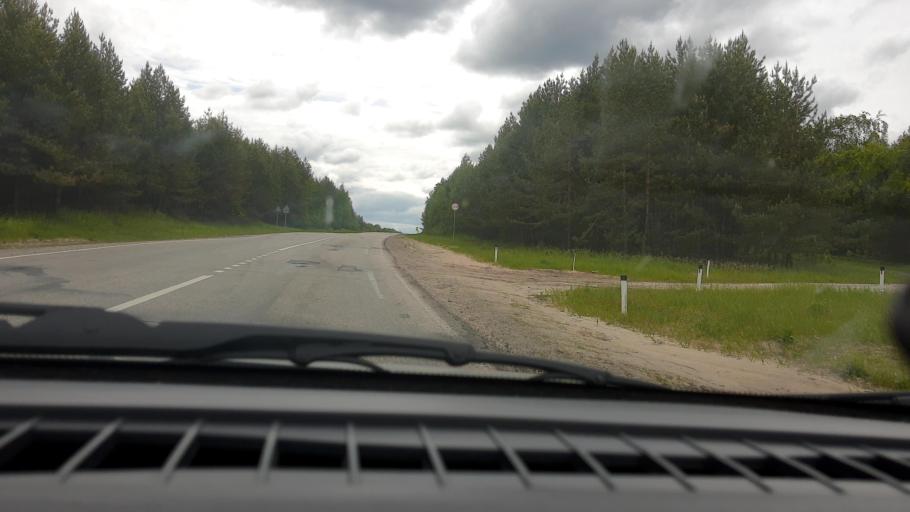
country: RU
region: Nizjnij Novgorod
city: Krasnyye Baki
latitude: 56.9854
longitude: 45.1179
